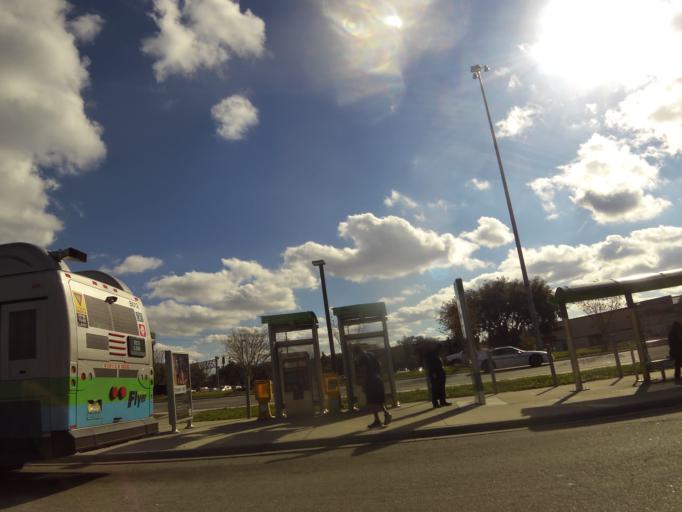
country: US
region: Florida
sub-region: Duval County
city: Jacksonville
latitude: 30.3219
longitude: -81.5525
